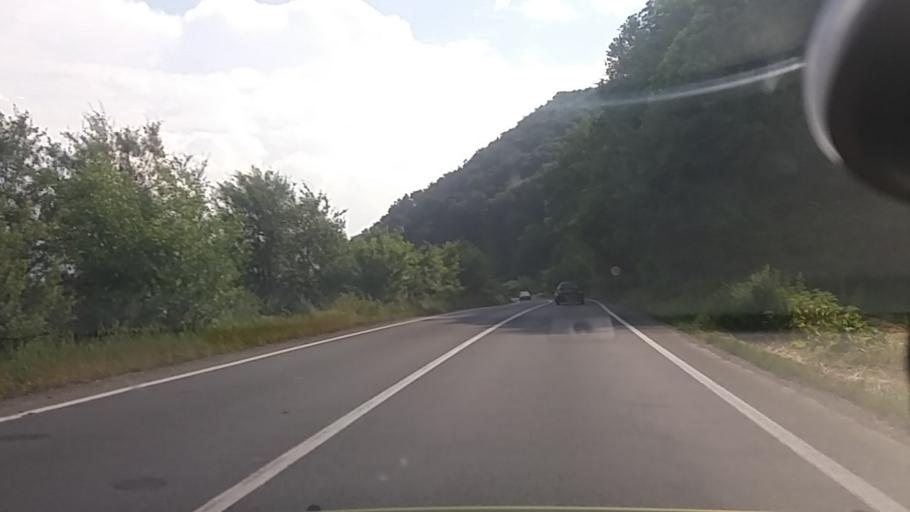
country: RO
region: Arad
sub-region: Comuna Barzava
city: Barzava
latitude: 46.1114
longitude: 21.9527
